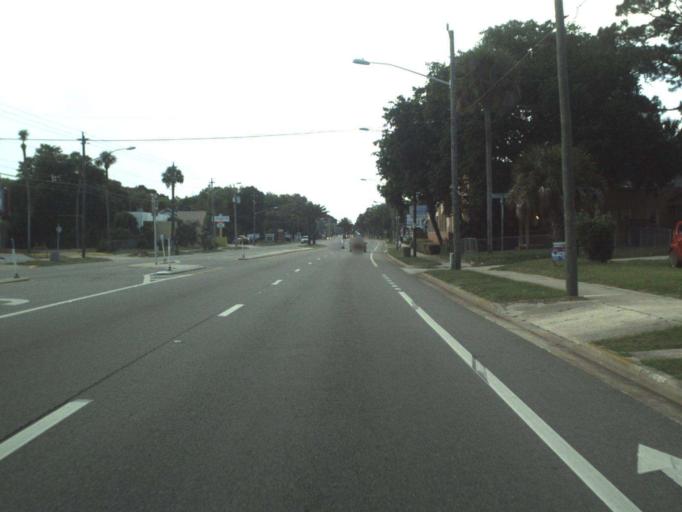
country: US
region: Florida
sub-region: Volusia County
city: Daytona Beach
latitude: 29.1917
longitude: -81.0125
